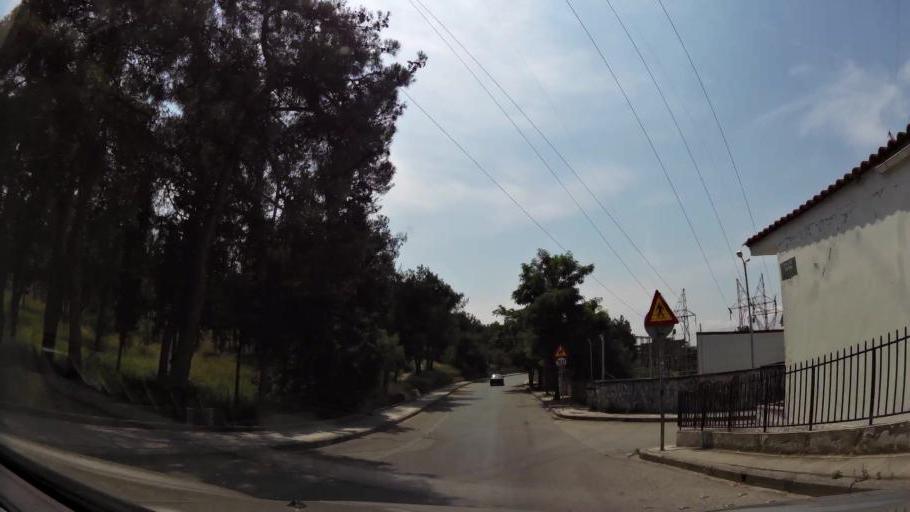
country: GR
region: Central Macedonia
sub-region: Nomos Thessalonikis
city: Triandria
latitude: 40.6284
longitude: 22.9692
